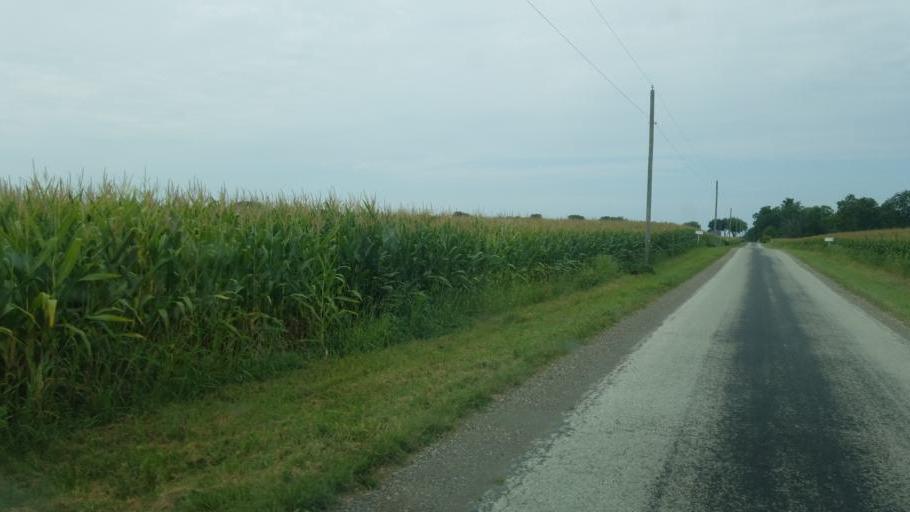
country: US
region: Ohio
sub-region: Marion County
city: Marion
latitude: 40.5129
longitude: -83.1243
